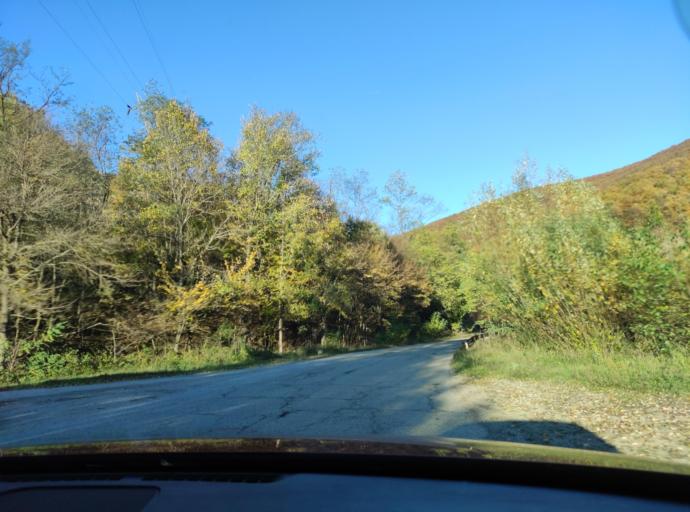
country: BG
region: Montana
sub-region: Obshtina Chiprovtsi
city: Chiprovtsi
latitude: 43.4034
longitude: 22.9364
